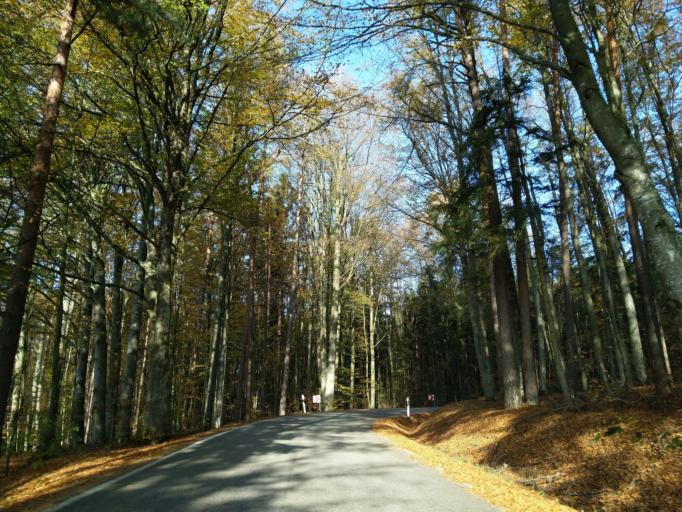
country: DE
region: Bavaria
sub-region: Lower Bavaria
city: Grattersdorf
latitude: 48.7942
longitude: 13.1773
